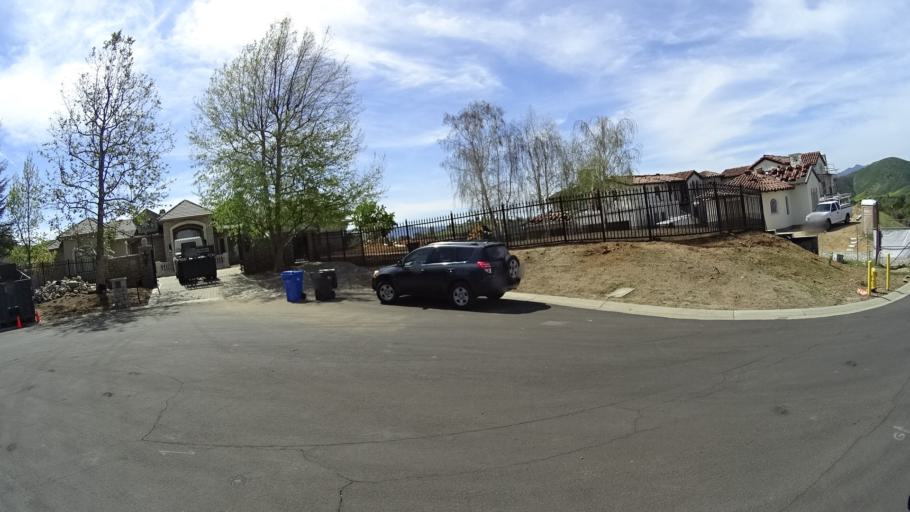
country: US
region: California
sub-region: Ventura County
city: Thousand Oaks
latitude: 34.2008
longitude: -118.8112
